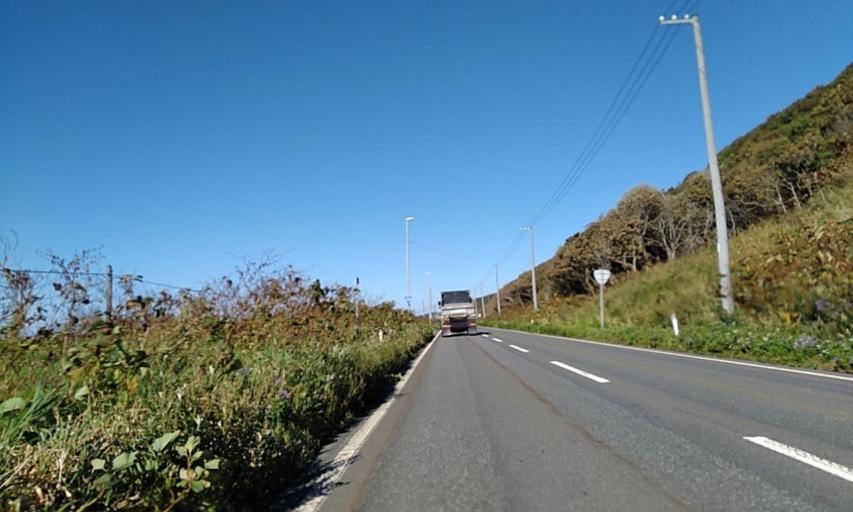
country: JP
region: Hokkaido
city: Shizunai-furukawacho
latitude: 42.4657
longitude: 142.1478
